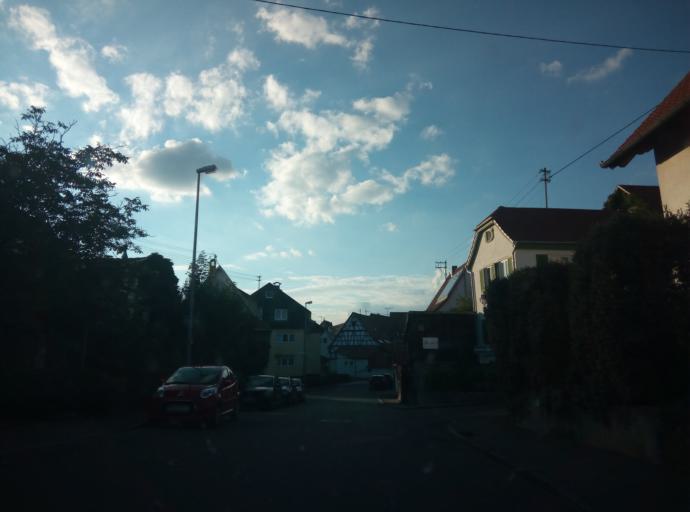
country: DE
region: Baden-Wuerttemberg
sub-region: Tuebingen Region
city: Kusterdingen
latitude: 48.5005
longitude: 9.1267
